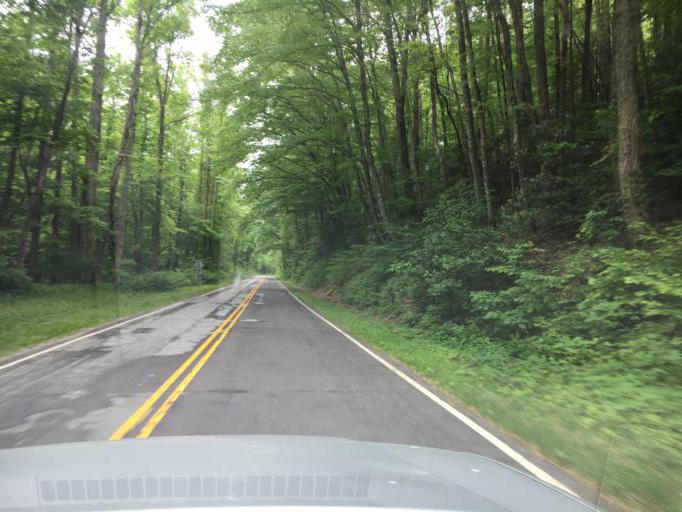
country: US
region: North Carolina
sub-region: Henderson County
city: Flat Rock
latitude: 35.1838
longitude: -82.4131
